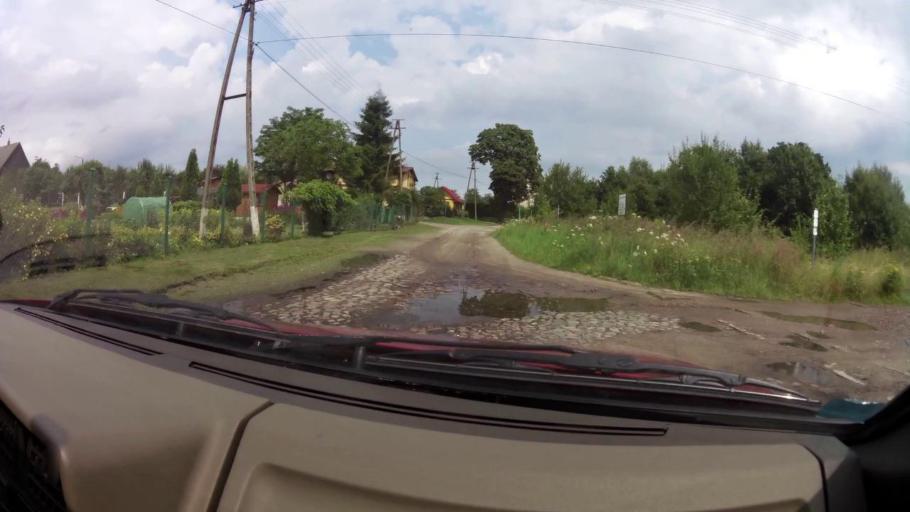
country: PL
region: West Pomeranian Voivodeship
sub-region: Powiat swidwinski
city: Polczyn-Zdroj
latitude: 53.7946
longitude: 16.0434
